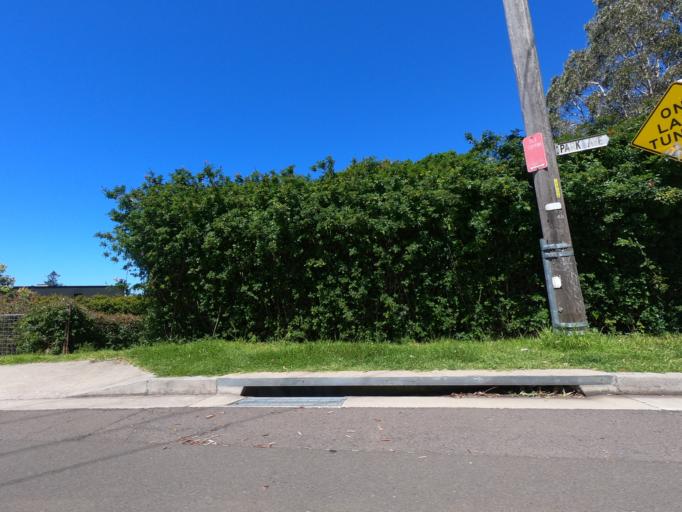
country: AU
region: New South Wales
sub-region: Wollongong
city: Bulli
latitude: -34.3041
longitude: 150.9332
